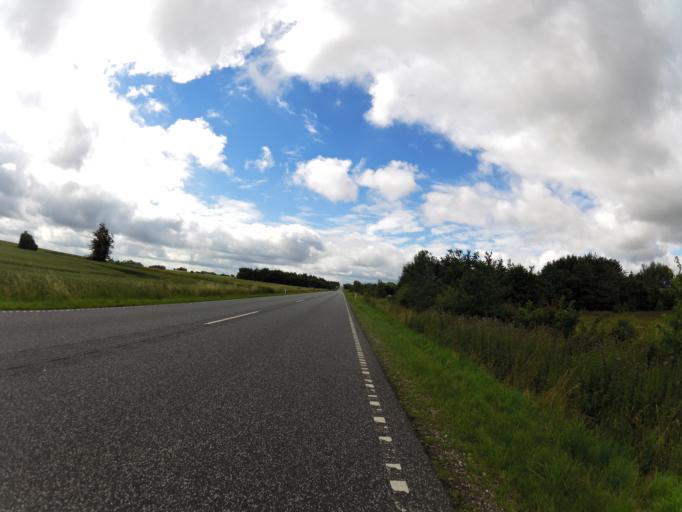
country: DK
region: North Denmark
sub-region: Mariagerfjord Kommune
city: Hadsund
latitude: 56.6058
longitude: 10.1465
